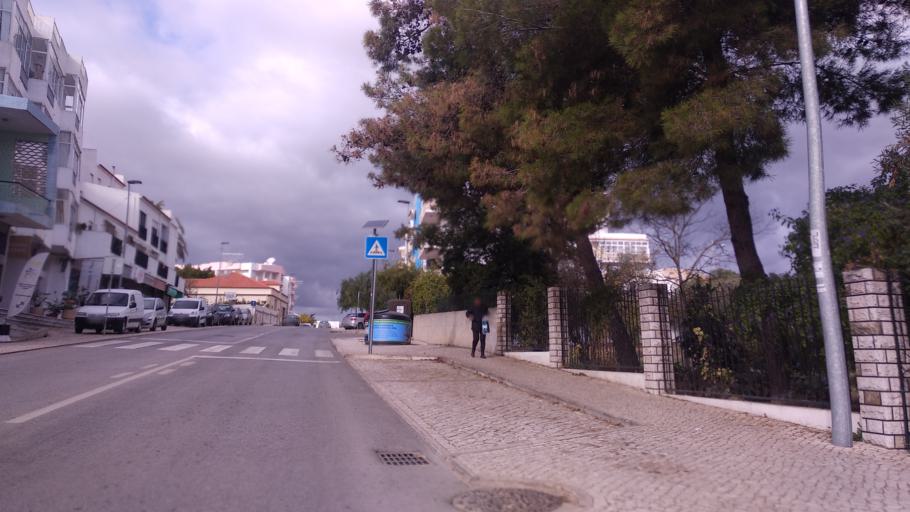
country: PT
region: Faro
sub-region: Loule
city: Almancil
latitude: 37.0882
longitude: -8.0339
